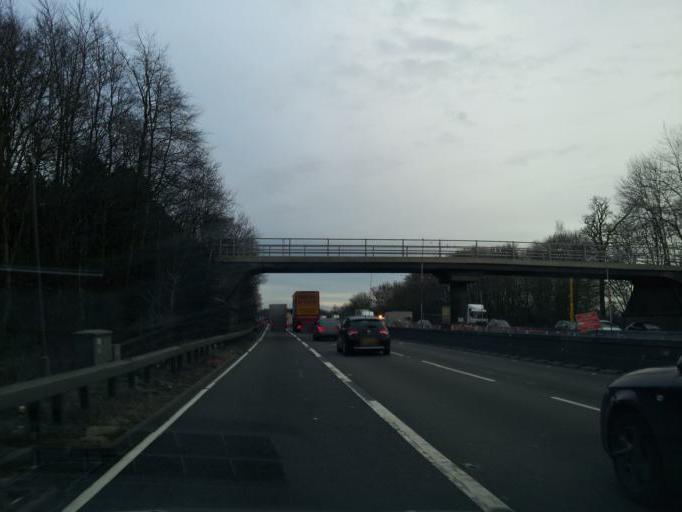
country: GB
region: England
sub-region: Northamptonshire
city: Long Buckby
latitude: 52.2595
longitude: -1.0843
